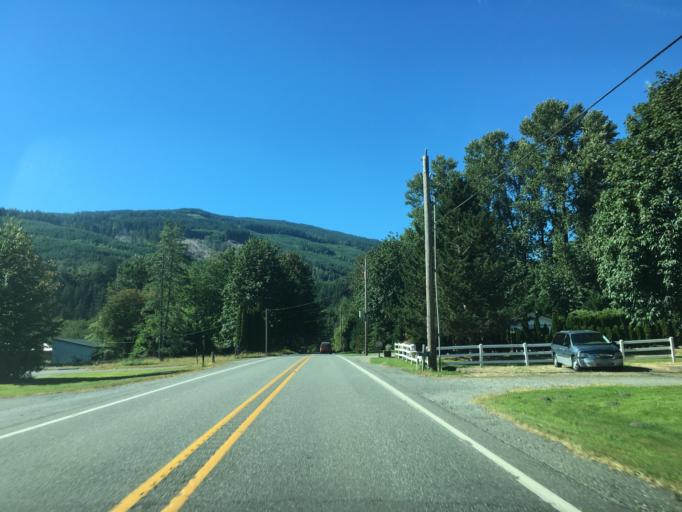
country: US
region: Washington
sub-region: Skagit County
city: Sedro-Woolley
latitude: 48.5982
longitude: -122.2309
